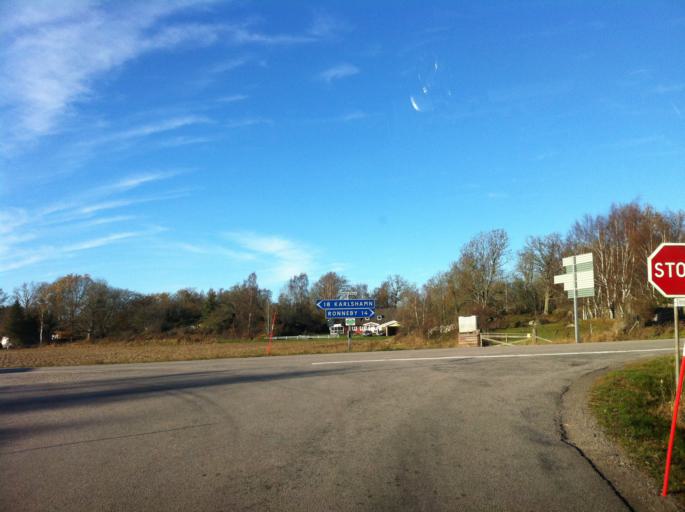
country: SE
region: Blekinge
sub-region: Ronneby Kommun
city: Brakne-Hoby
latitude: 56.2068
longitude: 15.0984
